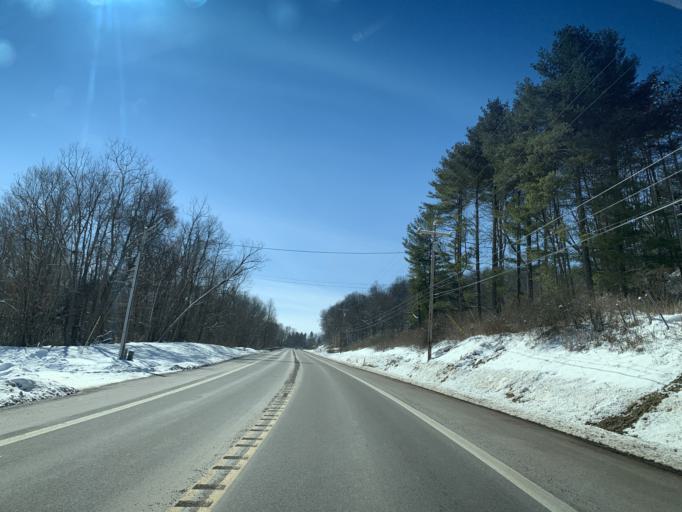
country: US
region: West Virginia
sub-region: Preston County
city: Terra Alta
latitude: 39.6617
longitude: -79.4318
